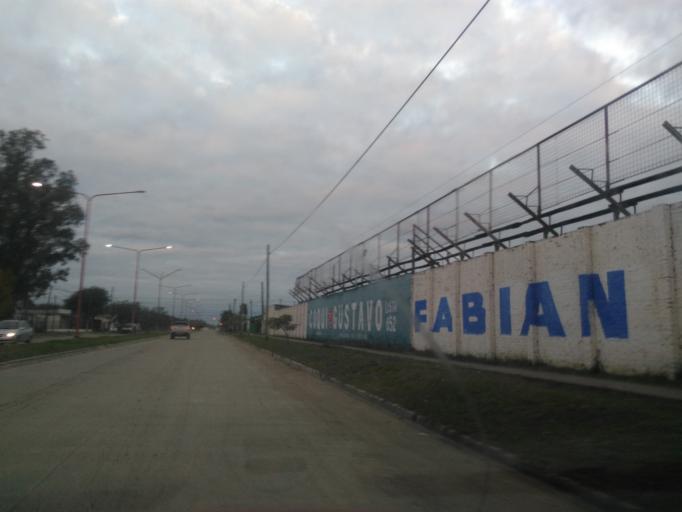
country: AR
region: Chaco
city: Resistencia
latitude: -27.4769
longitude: -58.9958
